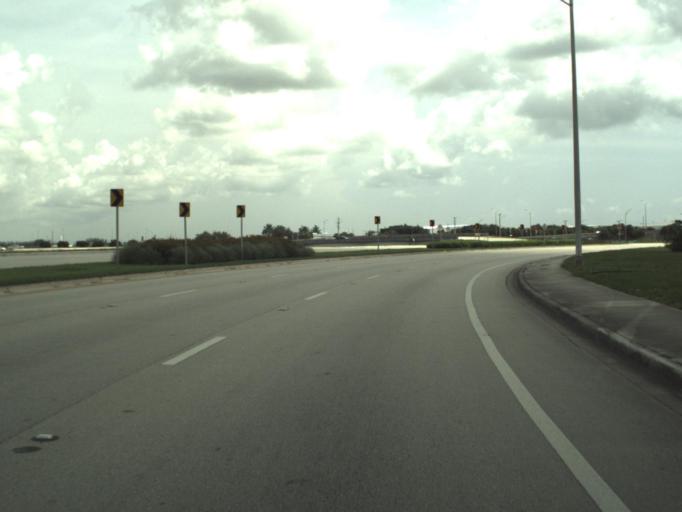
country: US
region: Florida
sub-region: Palm Beach County
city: Lake Clarke Shores
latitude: 26.6738
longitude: -80.0874
